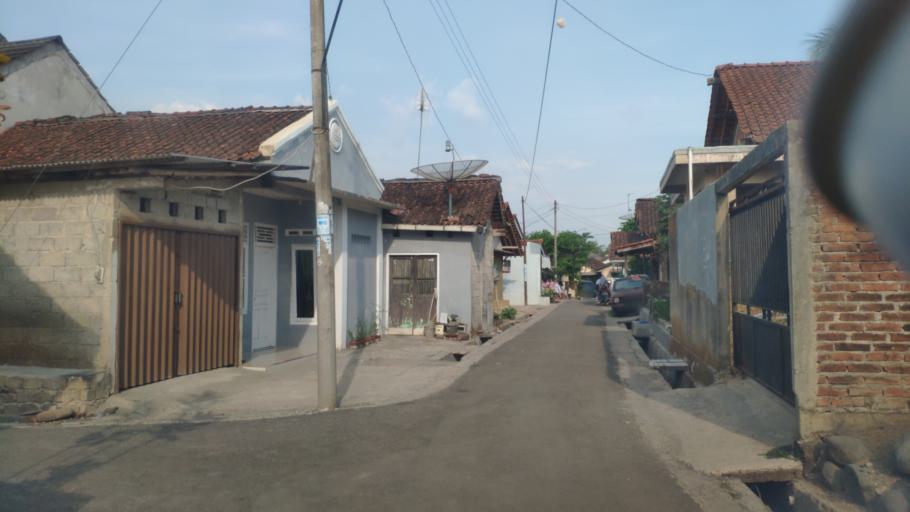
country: ID
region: Central Java
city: Wonosobo
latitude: -7.3896
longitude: 109.7182
